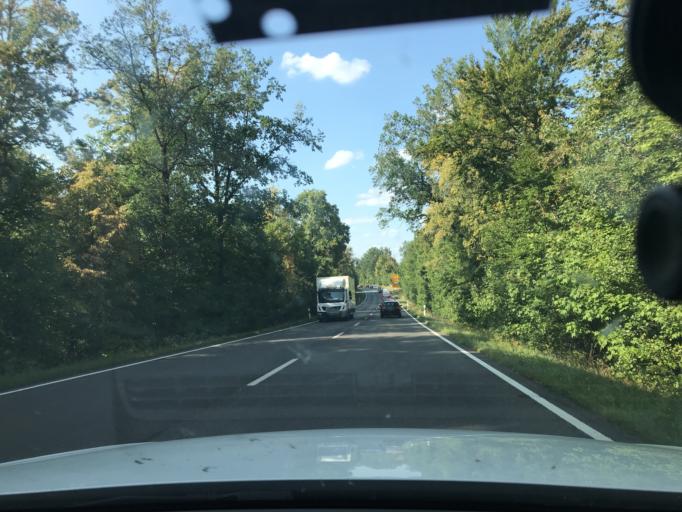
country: DE
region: Bavaria
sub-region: Upper Palatinate
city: Sulzbach-Rosenberg
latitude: 49.4914
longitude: 11.7319
